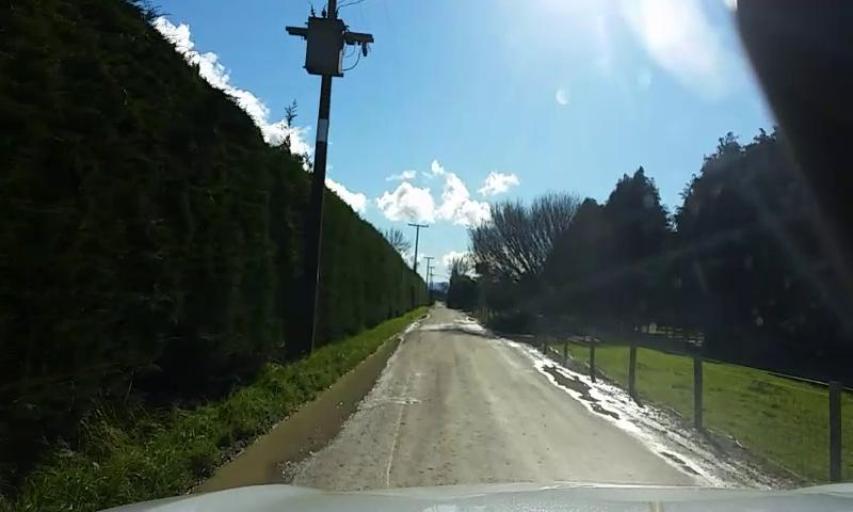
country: NZ
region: Tasman
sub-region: Tasman District
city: Richmond
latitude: -41.3029
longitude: 173.1445
